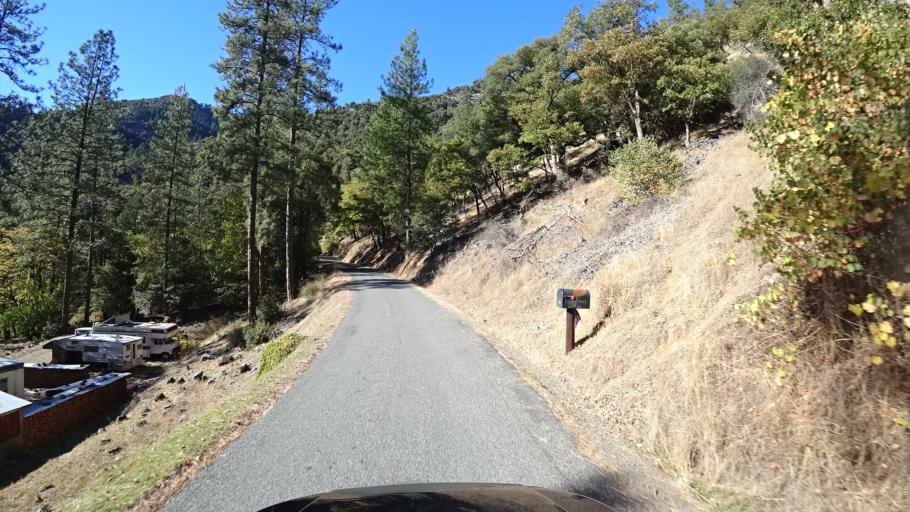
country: US
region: California
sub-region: Humboldt County
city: Willow Creek
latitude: 41.2831
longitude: -123.2608
